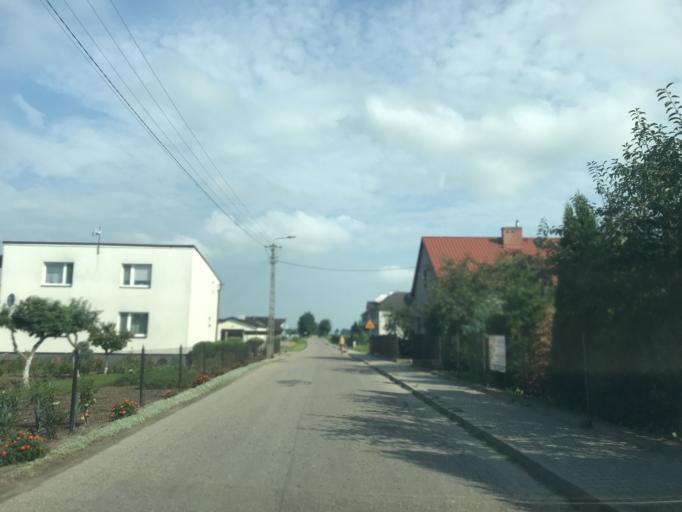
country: PL
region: Kujawsko-Pomorskie
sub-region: Powiat brodnicki
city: Brzozie
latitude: 53.3258
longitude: 19.6065
